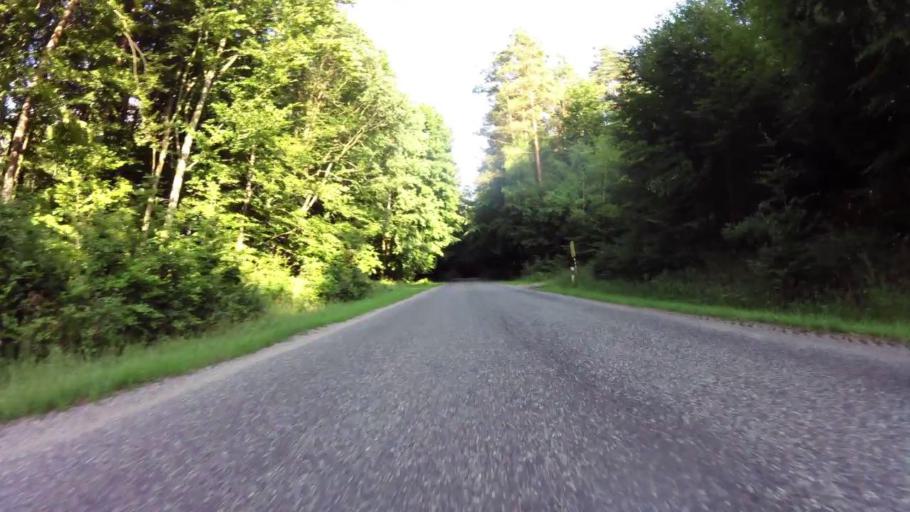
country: PL
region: West Pomeranian Voivodeship
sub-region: Powiat drawski
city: Drawsko Pomorskie
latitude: 53.4694
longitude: 15.8356
